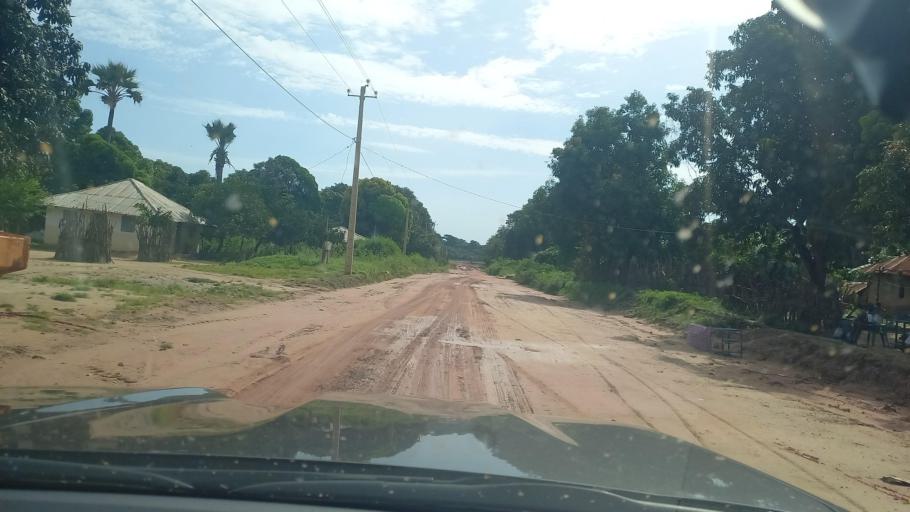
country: SN
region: Ziguinchor
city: Ziguinchor
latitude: 12.6734
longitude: -16.2086
